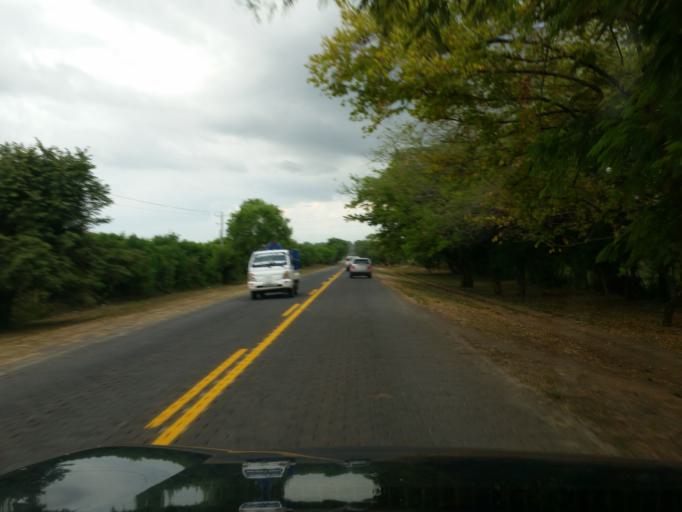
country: NI
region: Managua
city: Carlos Fonseca Amador
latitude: 11.9115
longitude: -86.5086
